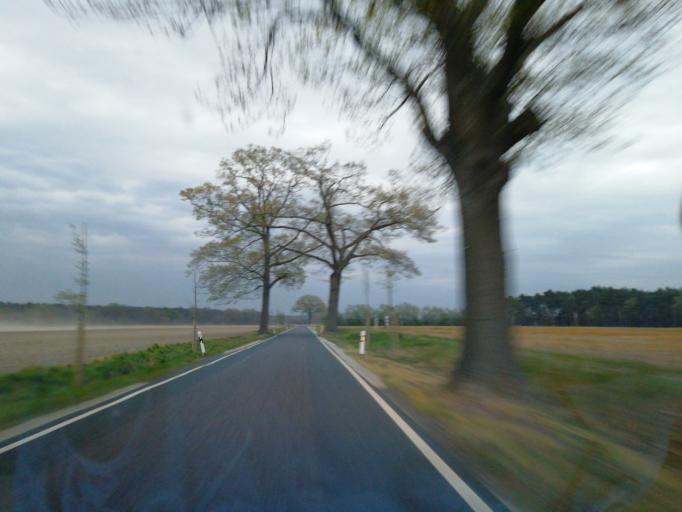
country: DE
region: Brandenburg
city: Calau
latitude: 51.7684
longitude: 13.8940
